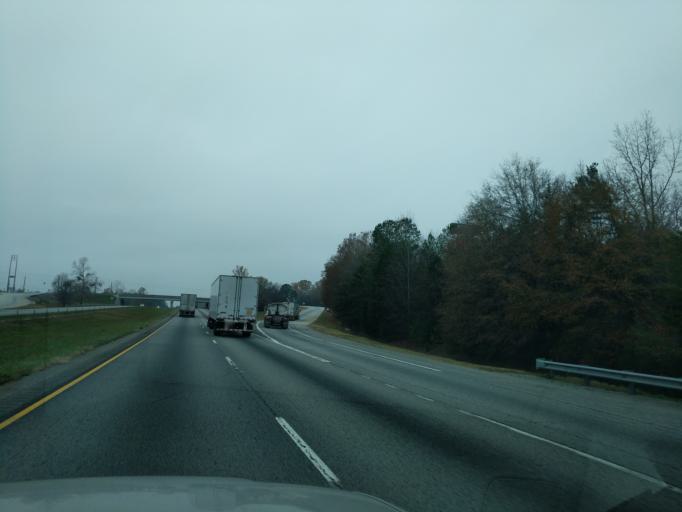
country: US
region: Georgia
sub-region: Franklin County
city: Carnesville
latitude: 34.3490
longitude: -83.3117
